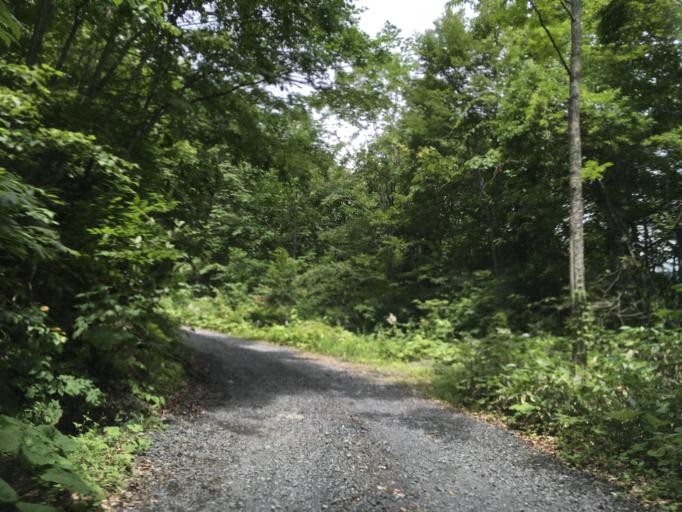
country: JP
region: Iwate
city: Ichinoseki
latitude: 38.9507
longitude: 140.8526
